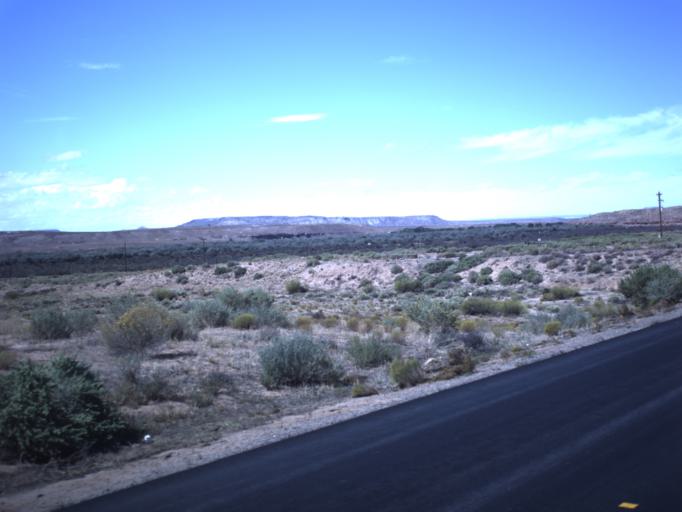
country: US
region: Utah
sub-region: San Juan County
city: Blanding
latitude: 37.2308
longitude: -109.2158
